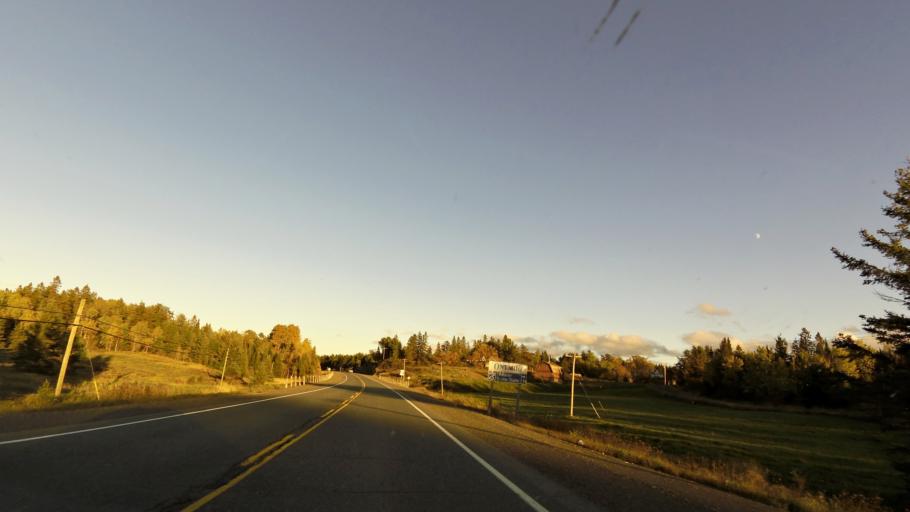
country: CA
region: Ontario
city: Espanola
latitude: 46.3320
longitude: -81.5037
